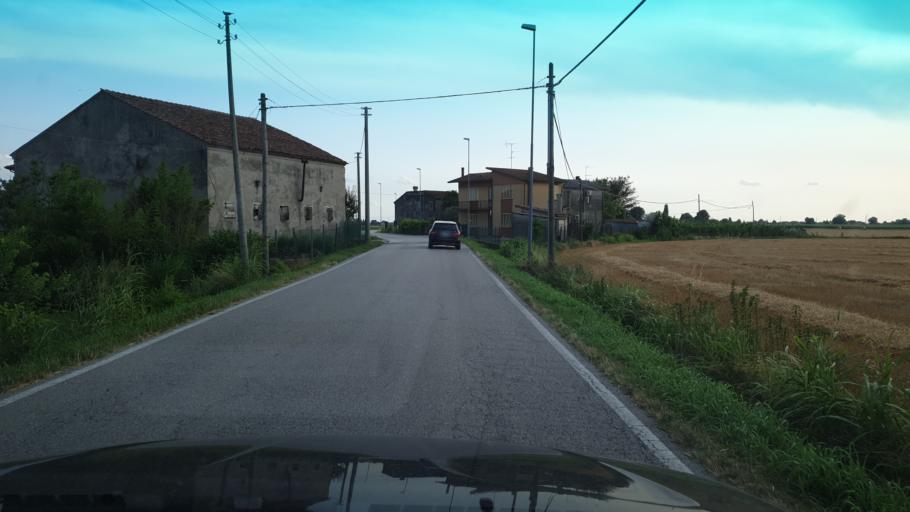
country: IT
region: Veneto
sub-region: Provincia di Rovigo
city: Castelguglielmo
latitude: 45.0135
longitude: 11.5292
